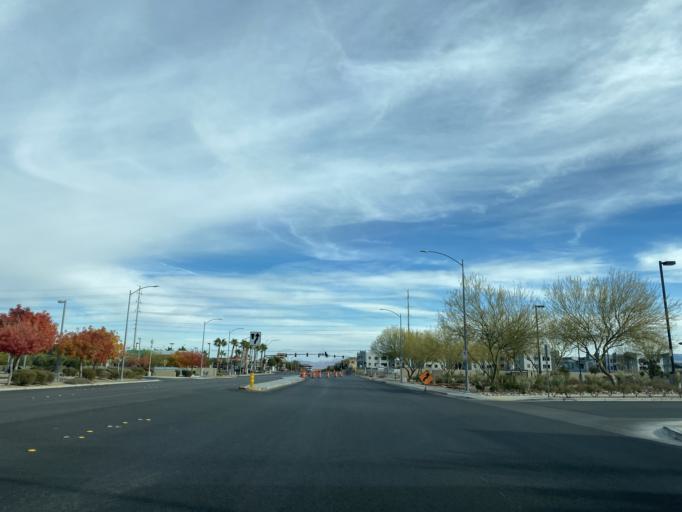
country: US
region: Nevada
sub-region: Clark County
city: Enterprise
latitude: 36.0412
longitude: -115.2458
